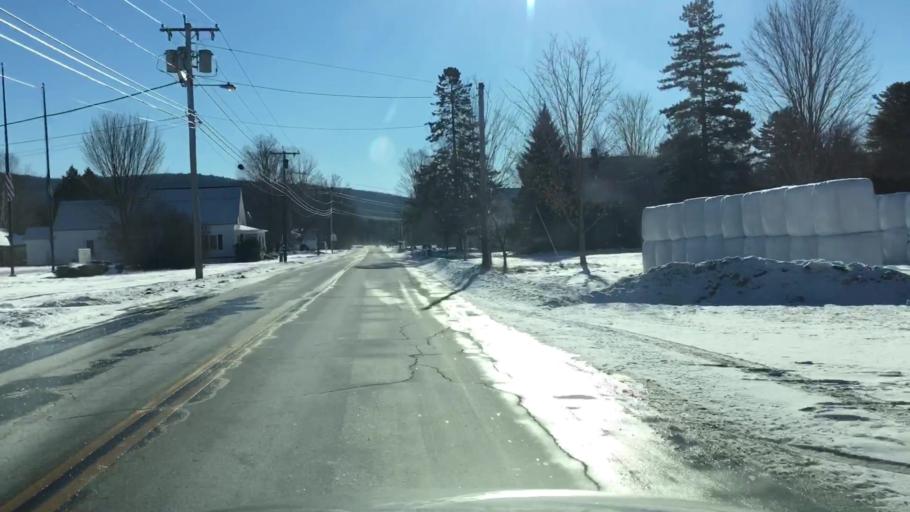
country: US
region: New Hampshire
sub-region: Grafton County
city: Woodsville
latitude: 44.2587
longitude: -72.0529
